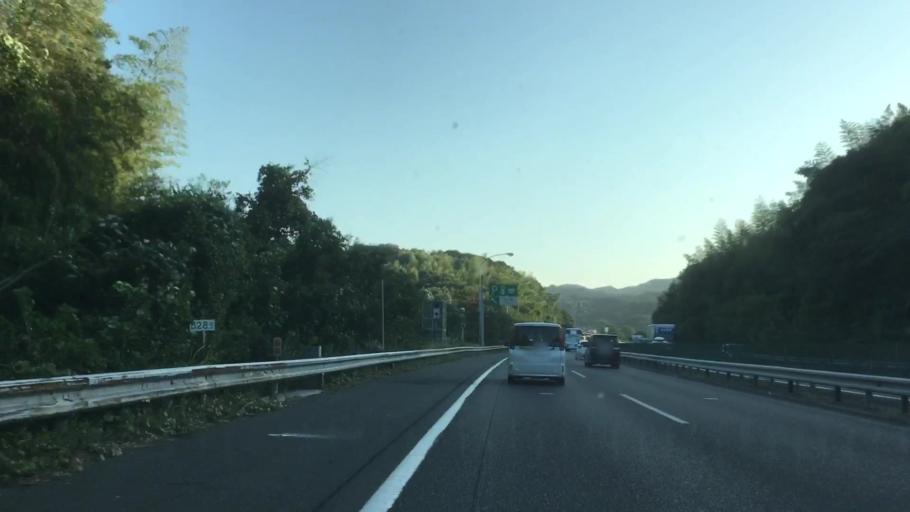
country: JP
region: Yamaguchi
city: Shimonoseki
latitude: 34.0543
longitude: 131.0066
